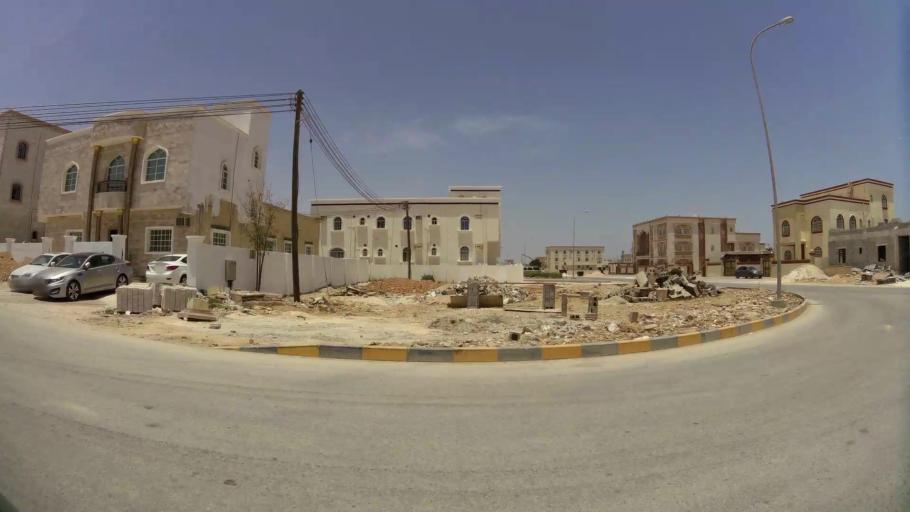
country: OM
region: Zufar
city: Salalah
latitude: 17.0738
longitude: 54.1583
